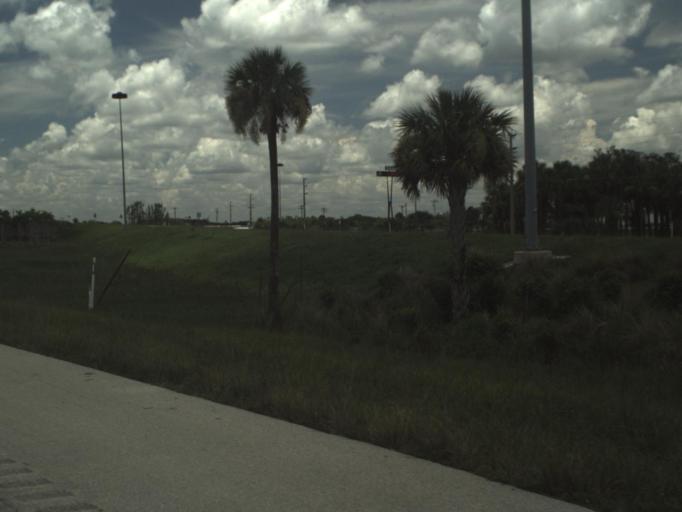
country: US
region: Florida
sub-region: Broward County
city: Weston
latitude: 26.1705
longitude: -80.8535
